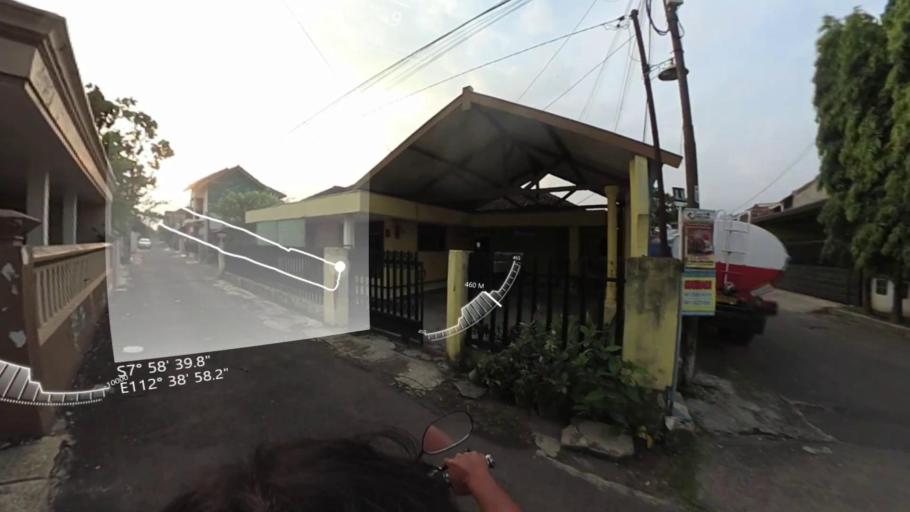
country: ID
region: East Java
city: Malang
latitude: -7.9777
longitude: 112.6495
